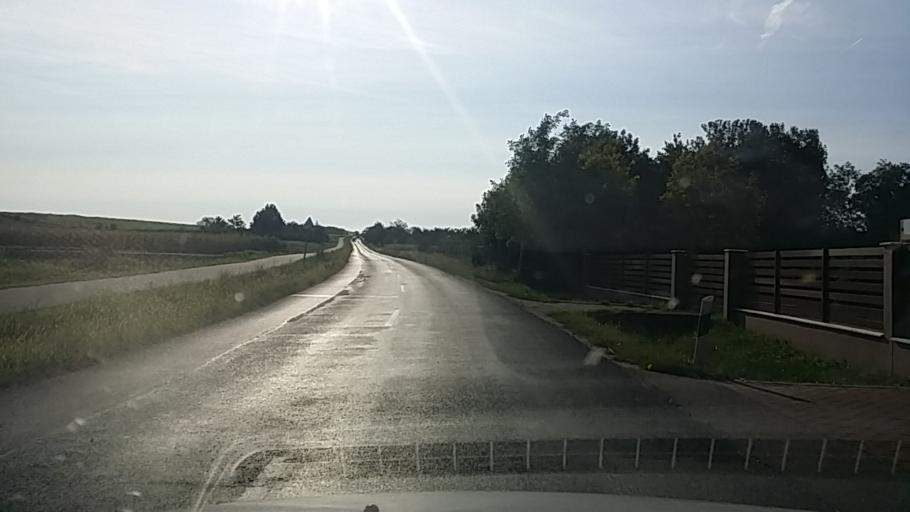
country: HU
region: Gyor-Moson-Sopron
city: Fertod
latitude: 47.6197
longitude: 16.8029
